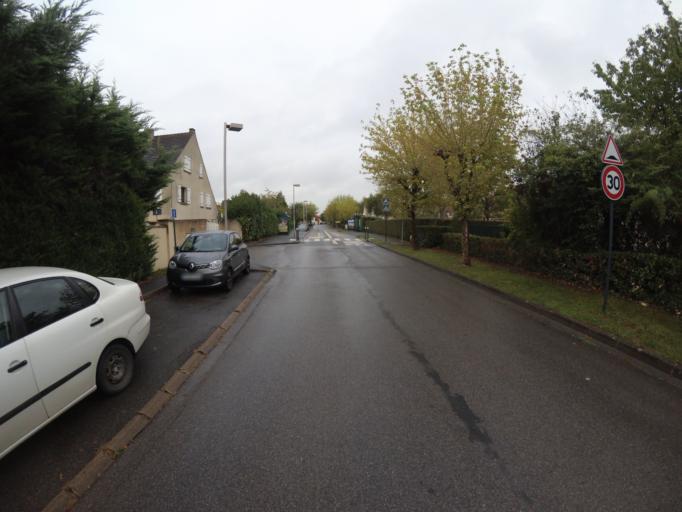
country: FR
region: Ile-de-France
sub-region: Departement de Seine-et-Marne
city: Chanteloup-en-Brie
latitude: 48.8529
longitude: 2.7391
